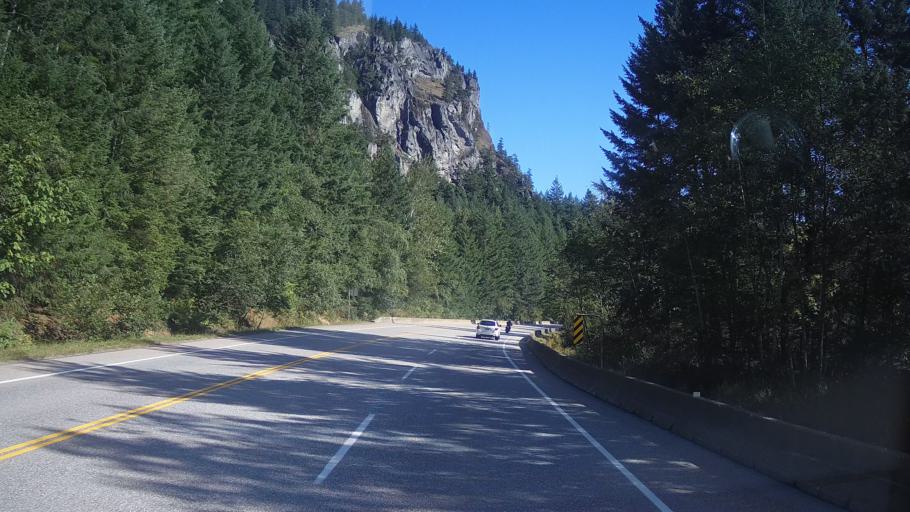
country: CA
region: British Columbia
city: Hope
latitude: 49.6444
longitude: -121.4106
